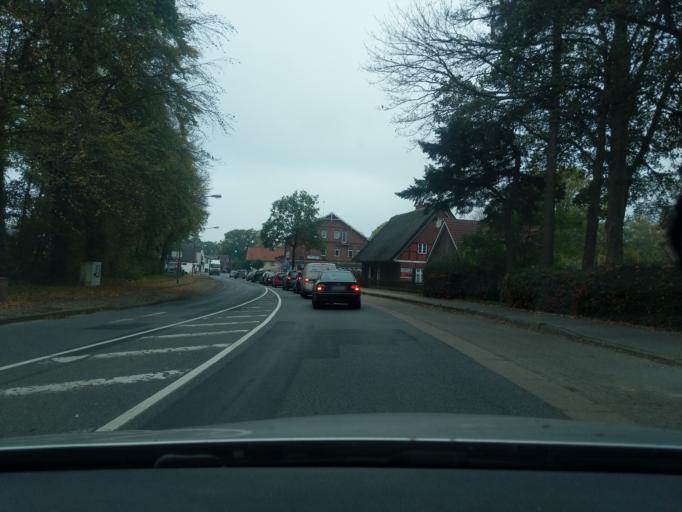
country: DE
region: Lower Saxony
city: Himmelpforten
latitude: 53.6126
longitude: 9.3118
